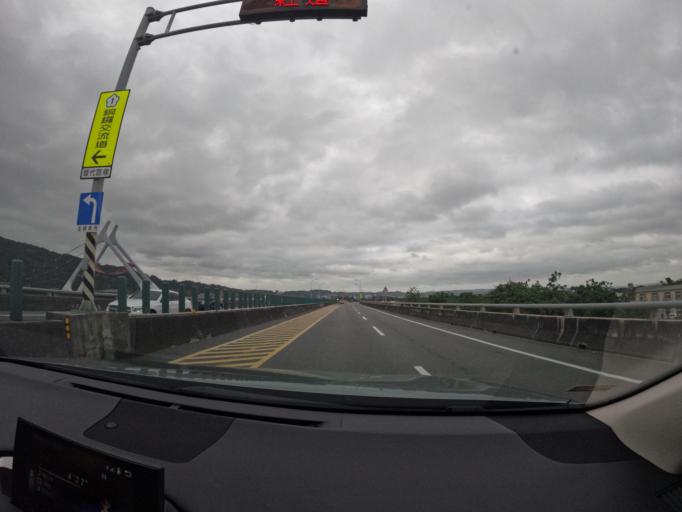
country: TW
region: Taiwan
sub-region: Miaoli
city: Miaoli
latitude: 24.4760
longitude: 120.8105
